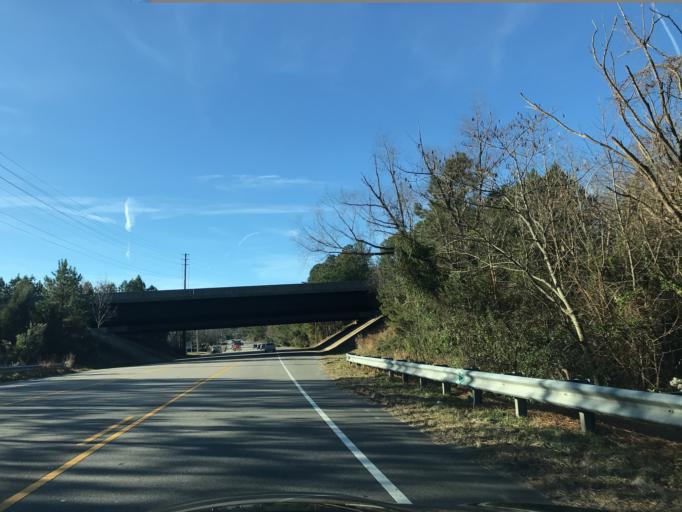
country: US
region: North Carolina
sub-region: Wake County
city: Wake Forest
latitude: 35.8945
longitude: -78.6001
